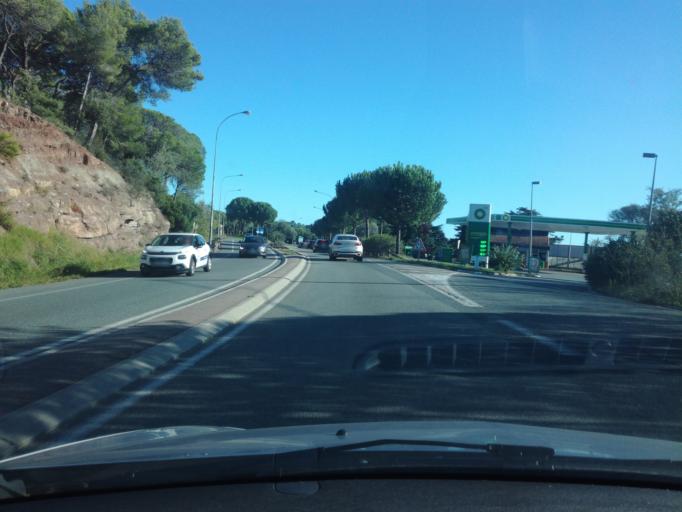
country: FR
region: Provence-Alpes-Cote d'Azur
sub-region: Departement du Var
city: Frejus
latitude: 43.4610
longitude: 6.7423
